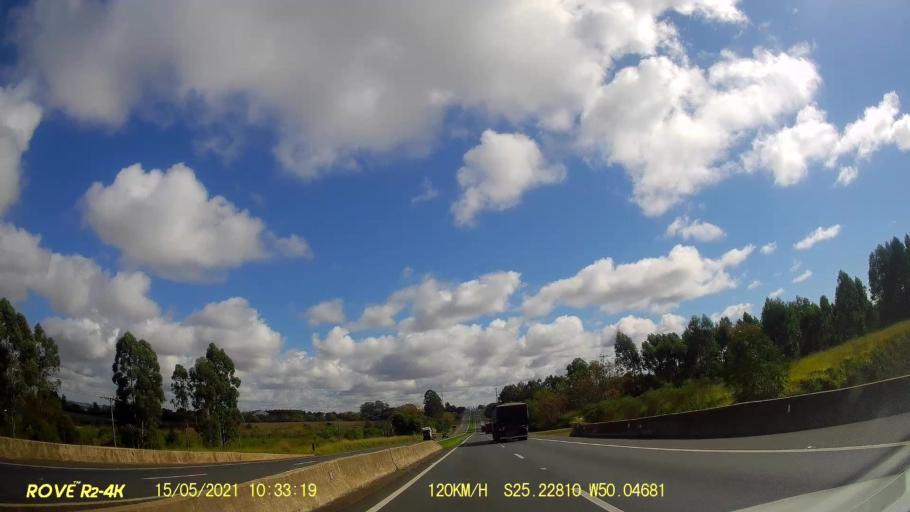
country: BR
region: Parana
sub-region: Ponta Grossa
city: Ponta Grossa
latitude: -25.2280
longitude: -50.0466
